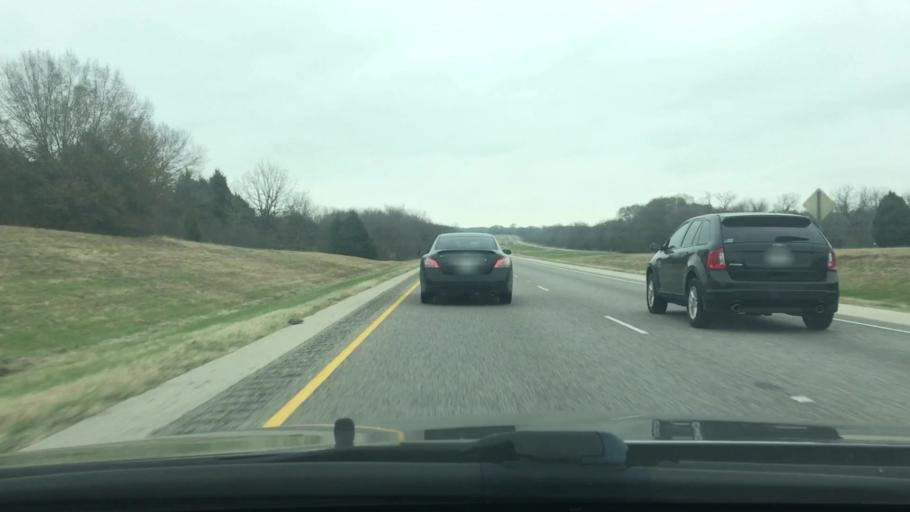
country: US
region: Texas
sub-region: Freestone County
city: Fairfield
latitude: 31.8024
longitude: -96.2607
